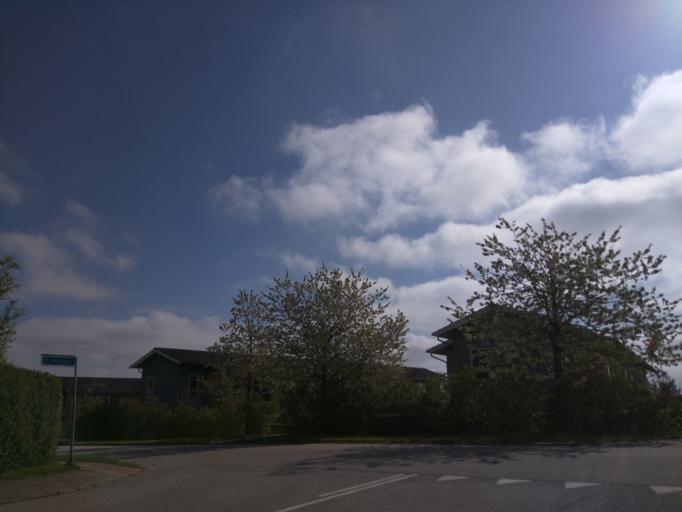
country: DK
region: Central Jutland
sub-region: Viborg Kommune
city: Viborg
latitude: 56.4403
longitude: 9.3952
